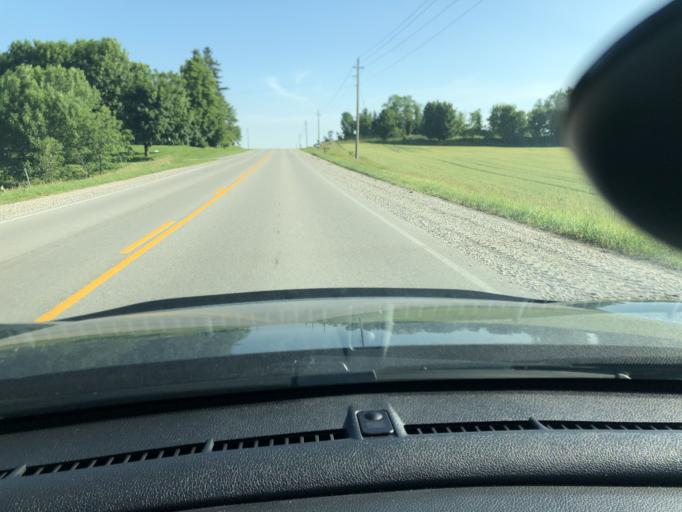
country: CA
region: Ontario
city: Stratford
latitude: 43.4102
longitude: -80.8378
